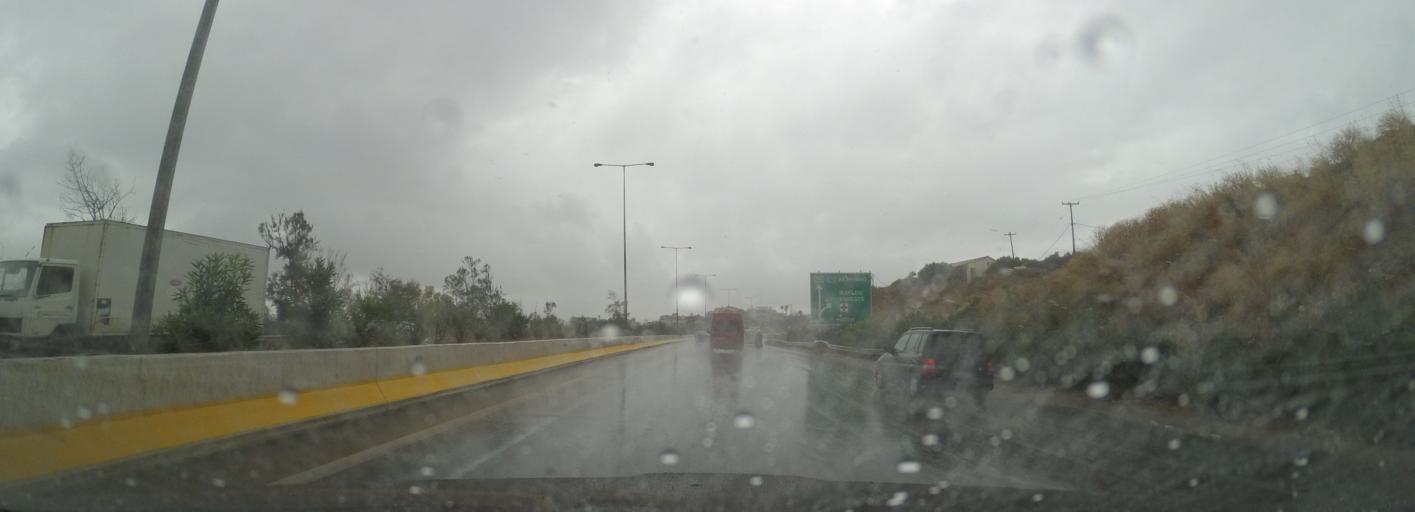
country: GR
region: Crete
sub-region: Nomos Irakleiou
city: Irakleion
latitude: 35.3240
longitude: 25.1501
